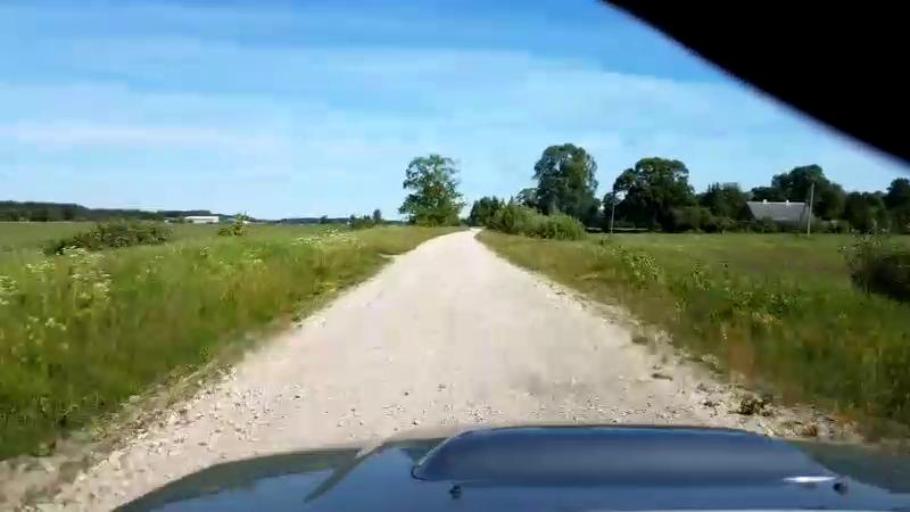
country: EE
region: Paernumaa
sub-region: Sauga vald
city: Sauga
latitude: 58.4748
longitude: 24.5328
